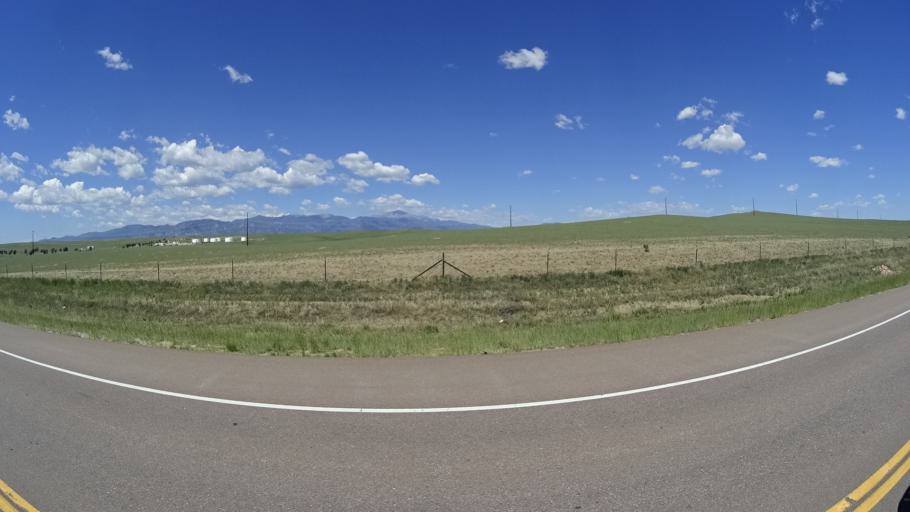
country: US
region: Colorado
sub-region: El Paso County
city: Security-Widefield
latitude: 38.7874
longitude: -104.6586
